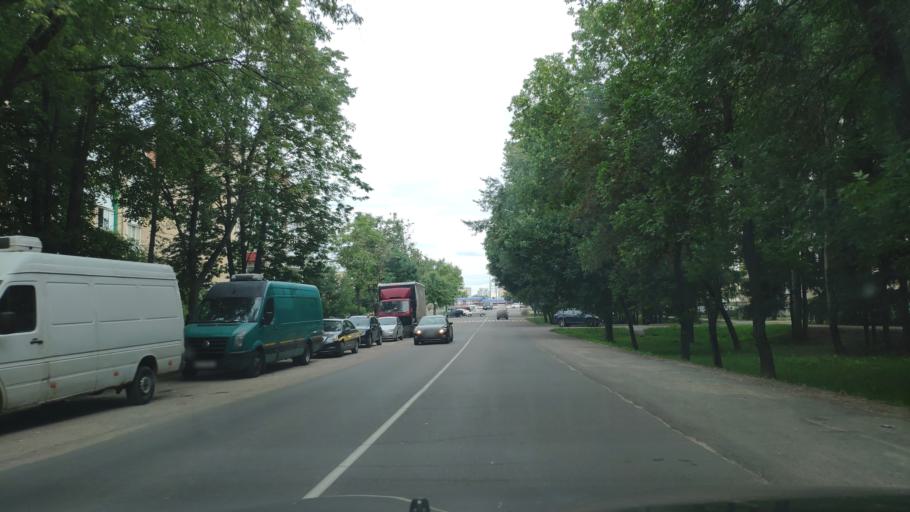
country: BY
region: Minsk
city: Zhdanovichy
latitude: 53.9496
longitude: 27.4286
